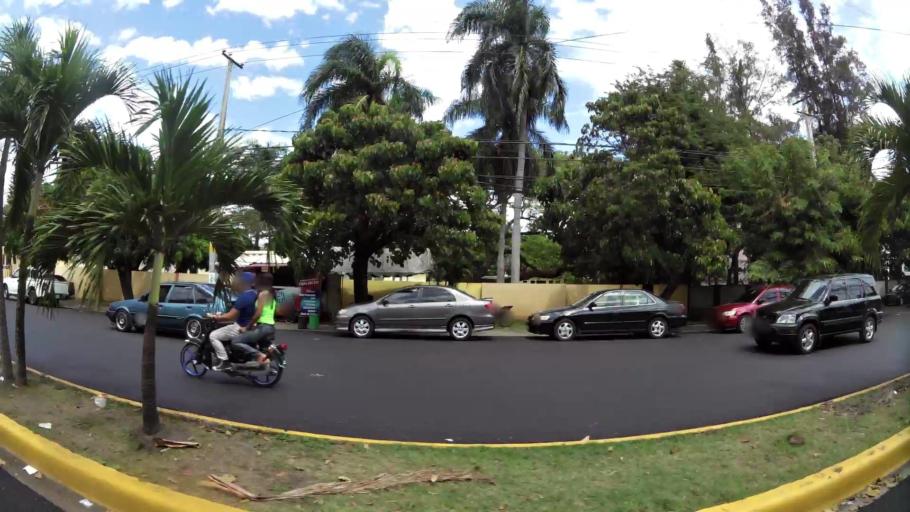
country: DO
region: Santiago
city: Santiago de los Caballeros
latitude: 19.4583
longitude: -70.6876
